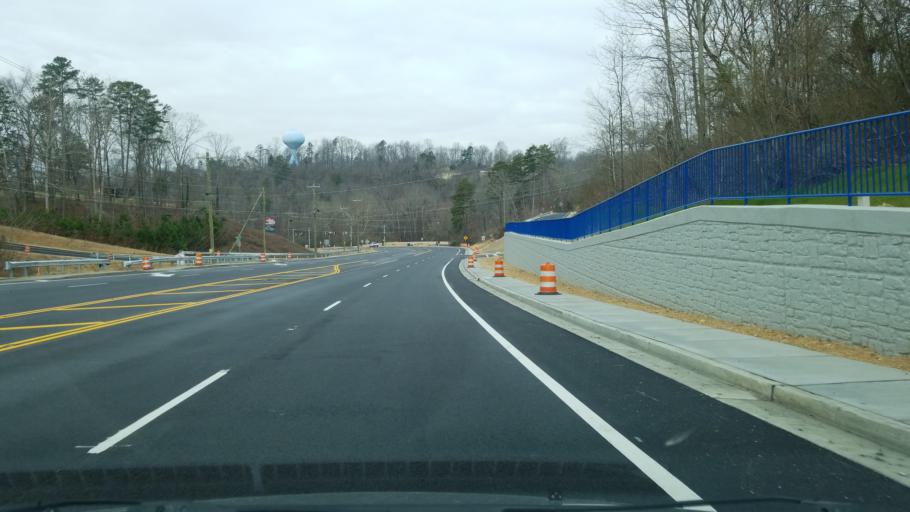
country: US
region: Tennessee
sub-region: Hamilton County
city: East Brainerd
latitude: 35.0043
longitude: -85.1176
